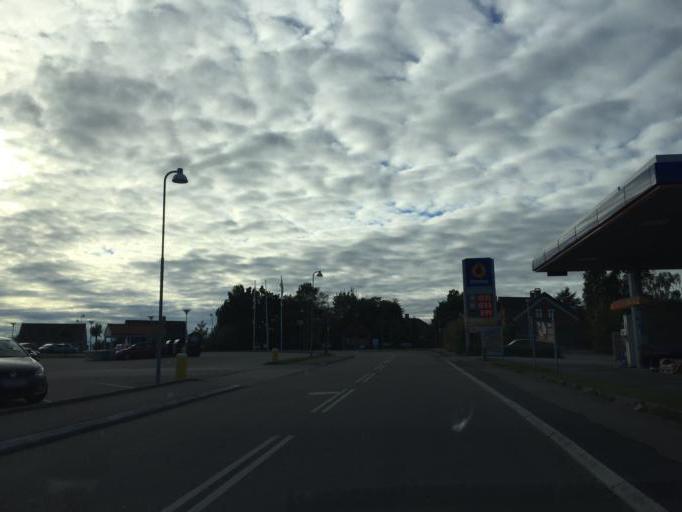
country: DK
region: Zealand
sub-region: Odsherred Kommune
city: Asnaes
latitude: 55.8129
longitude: 11.4998
